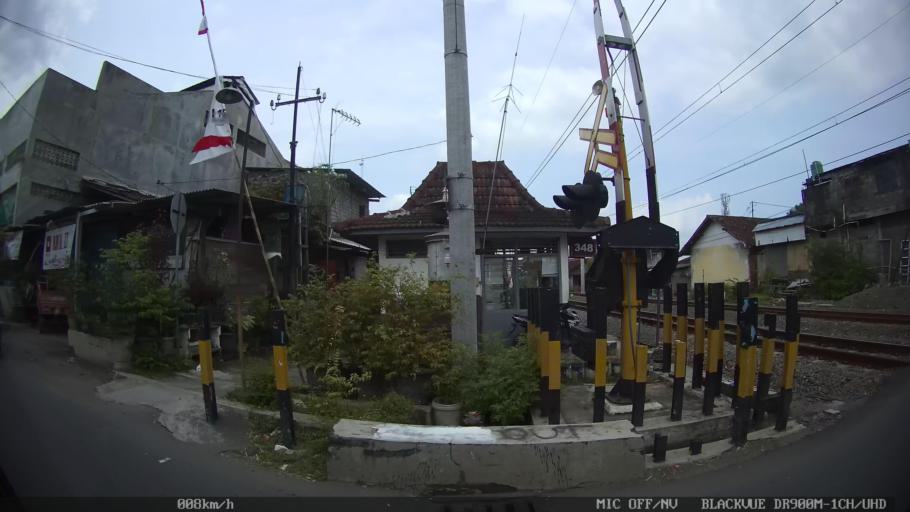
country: ID
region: Daerah Istimewa Yogyakarta
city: Yogyakarta
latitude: -7.7882
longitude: 110.3985
